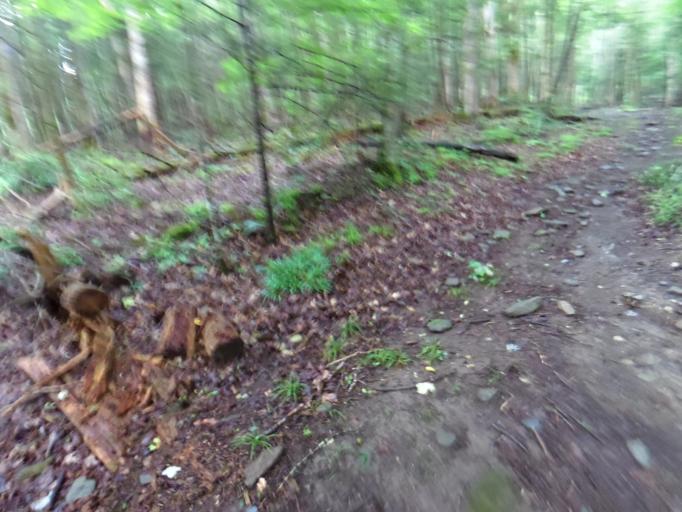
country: US
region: Tennessee
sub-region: Blount County
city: Wildwood
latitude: 35.6062
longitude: -83.7484
